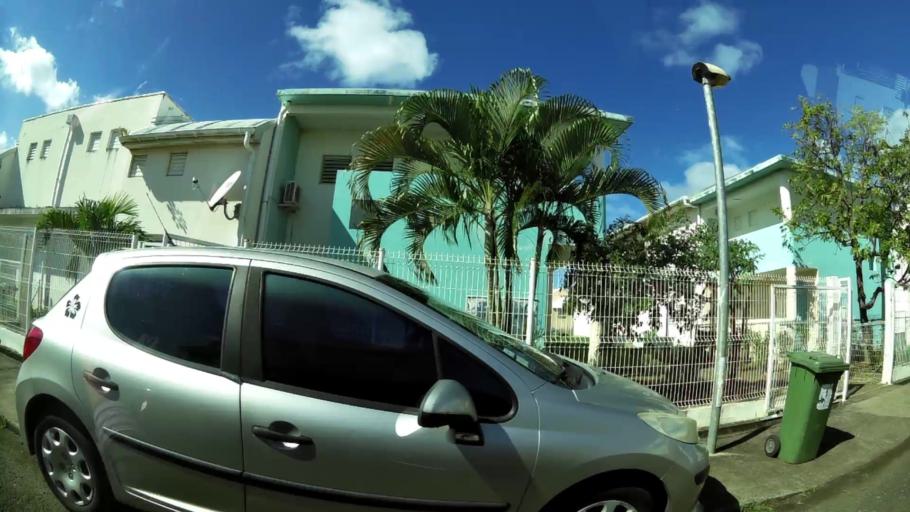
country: GP
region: Guadeloupe
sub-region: Guadeloupe
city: Port-Louis
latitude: 16.4126
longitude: -61.5272
